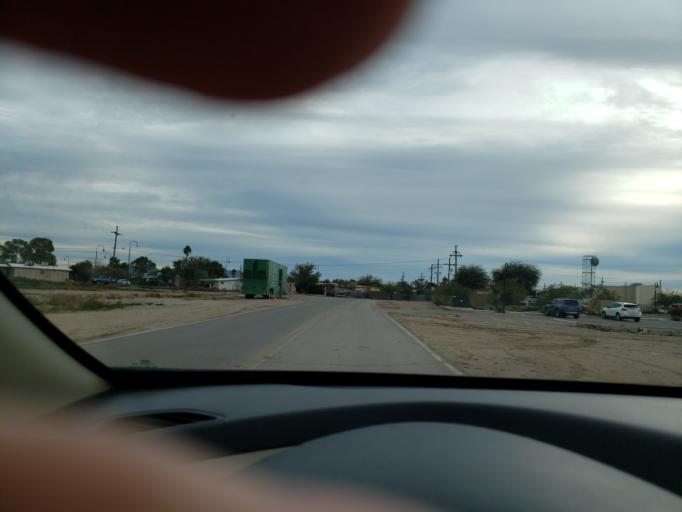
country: US
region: Arizona
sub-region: Pima County
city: Marana
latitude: 32.4576
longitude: -111.2161
